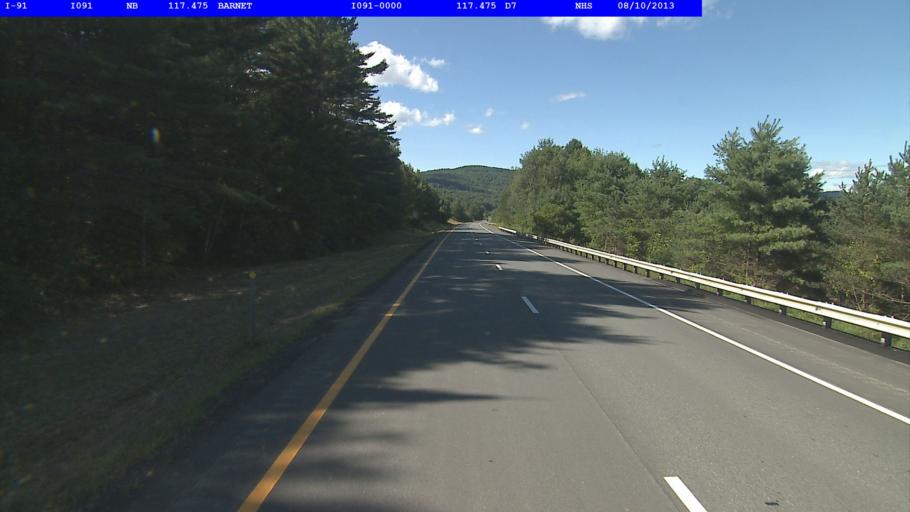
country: US
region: New Hampshire
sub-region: Grafton County
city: Woodsville
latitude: 44.2589
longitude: -72.0652
